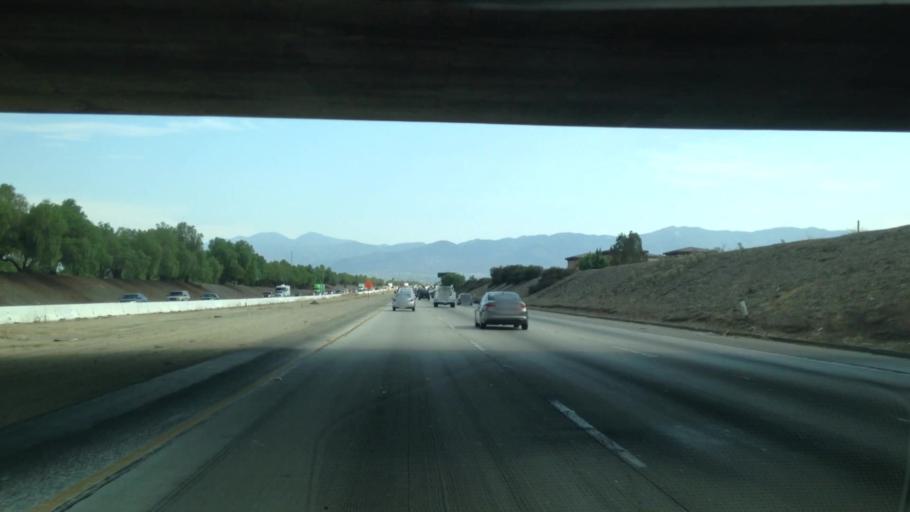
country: US
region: California
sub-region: Riverside County
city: Norco
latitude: 33.9244
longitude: -117.5567
